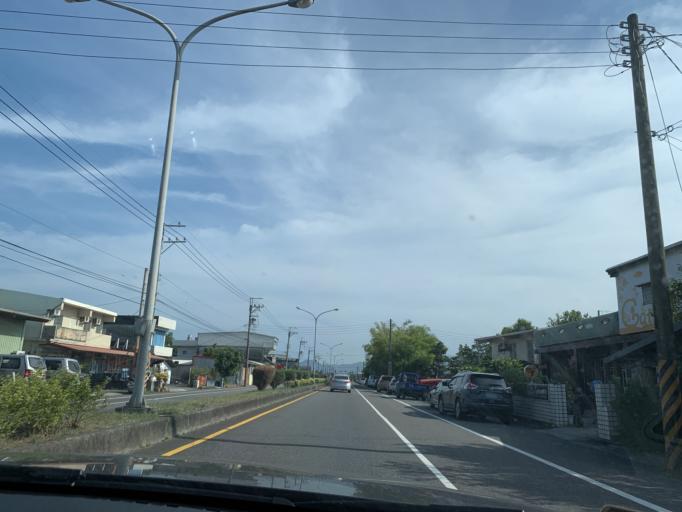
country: TW
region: Taiwan
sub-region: Yilan
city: Yilan
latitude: 24.7467
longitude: 121.8162
